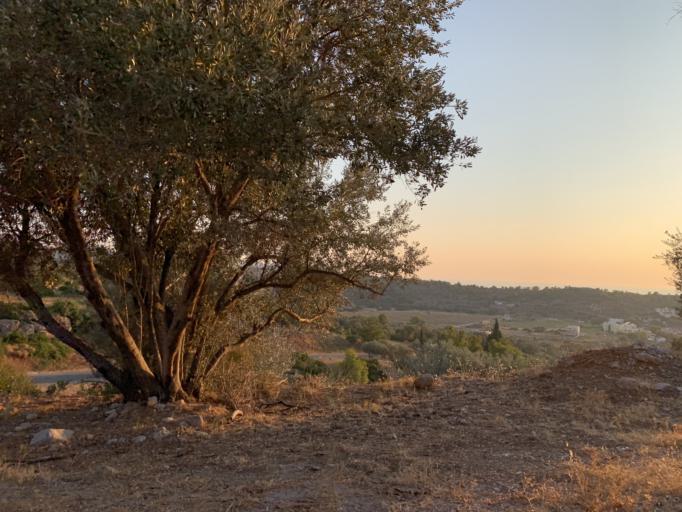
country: GR
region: North Aegean
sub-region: Chios
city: Thymiana
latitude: 38.3406
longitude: 25.9997
